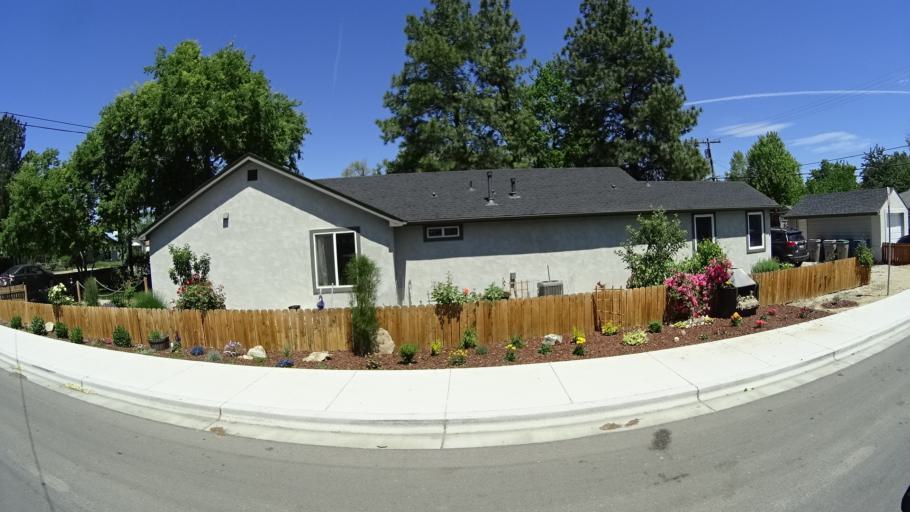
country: US
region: Idaho
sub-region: Ada County
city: Boise
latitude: 43.5825
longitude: -116.2233
